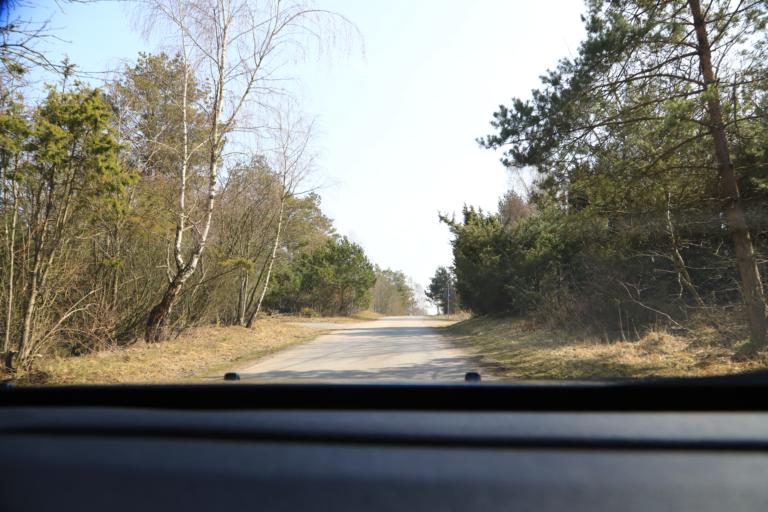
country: SE
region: Halland
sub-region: Kungsbacka Kommun
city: Frillesas
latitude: 57.2646
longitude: 12.1431
